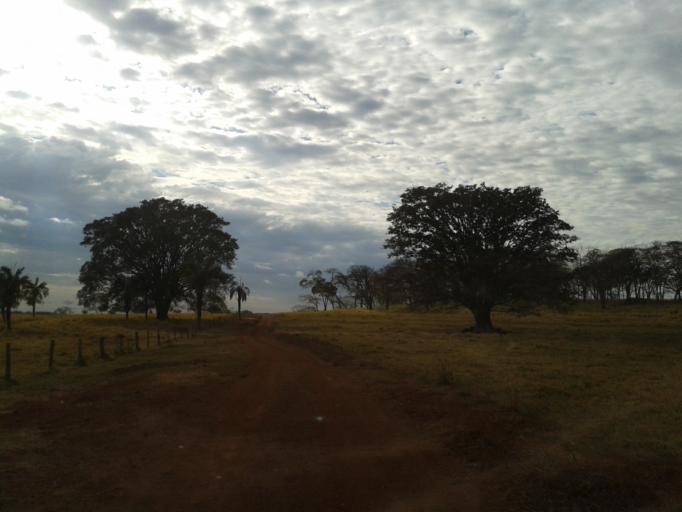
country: BR
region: Minas Gerais
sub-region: Santa Vitoria
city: Santa Vitoria
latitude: -18.7345
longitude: -50.2307
